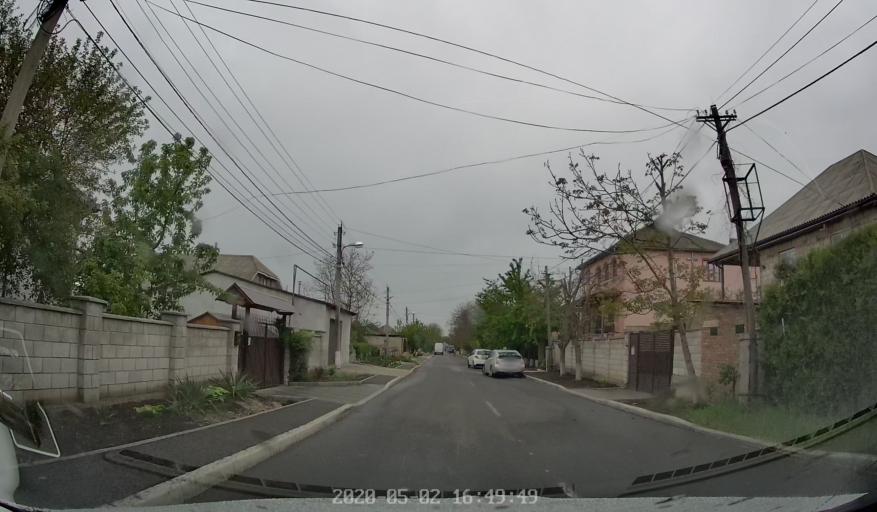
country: MD
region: Chisinau
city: Chisinau
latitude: 46.9682
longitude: 28.8278
